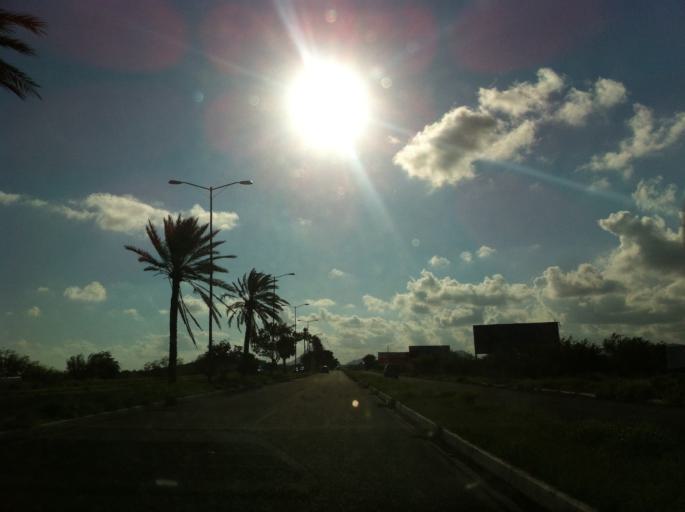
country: MX
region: Sonora
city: Heroica Guaymas
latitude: 27.9773
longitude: -110.9767
